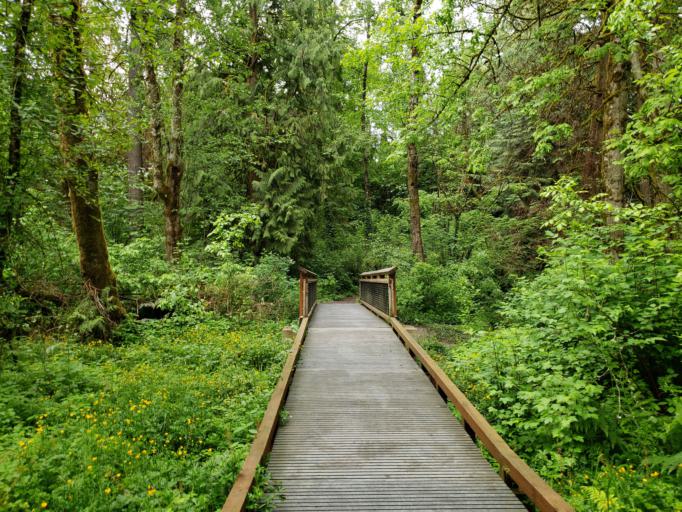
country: US
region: Oregon
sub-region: Washington County
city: Garden Home-Whitford
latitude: 45.4697
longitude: -122.7355
